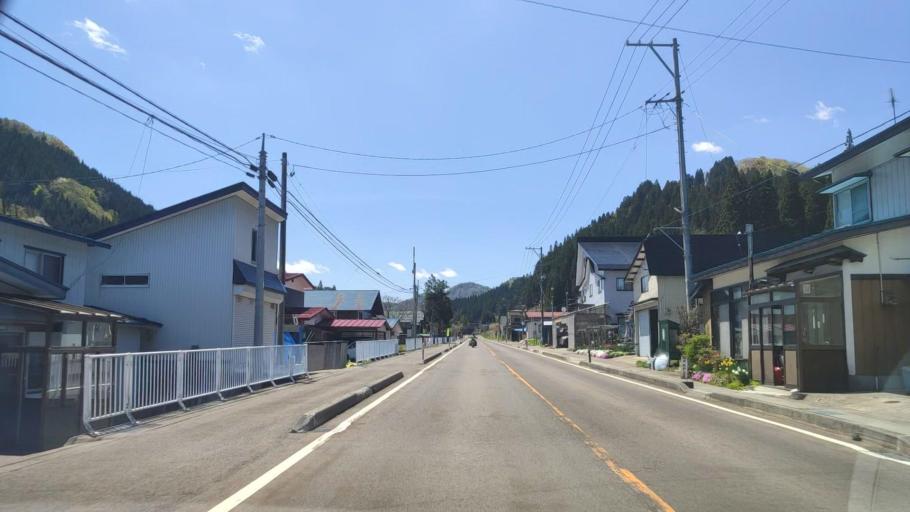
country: JP
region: Akita
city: Yuzawa
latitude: 39.0483
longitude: 140.3999
